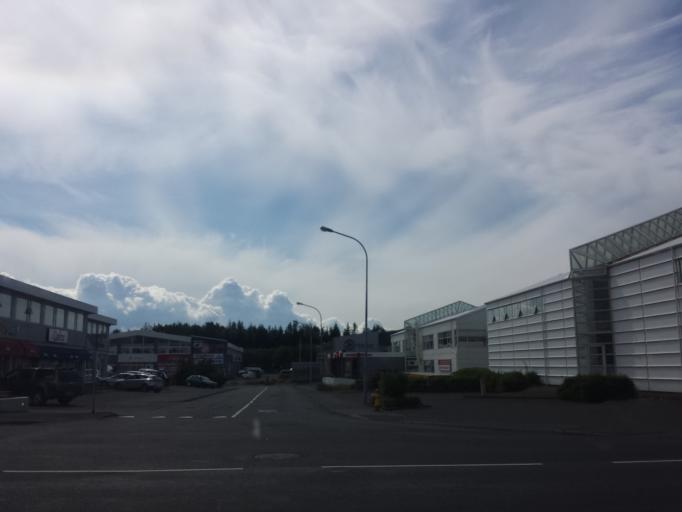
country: IS
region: Capital Region
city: Reykjavik
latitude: 64.1303
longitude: -21.8653
